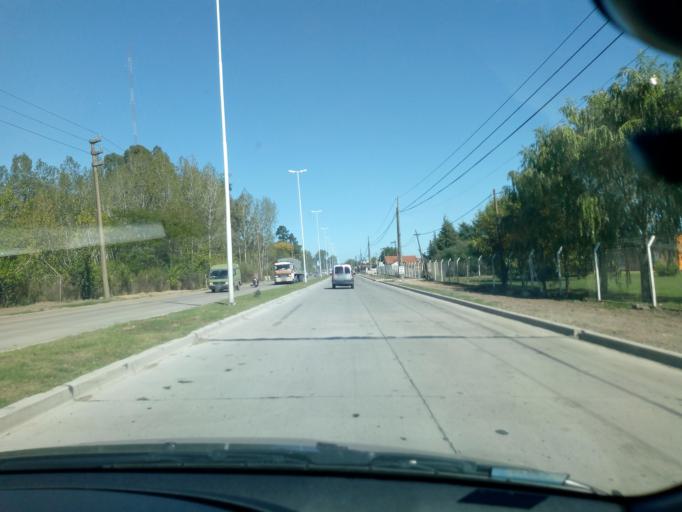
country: AR
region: Buenos Aires
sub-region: Partido de La Plata
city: La Plata
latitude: -34.9856
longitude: -58.0002
